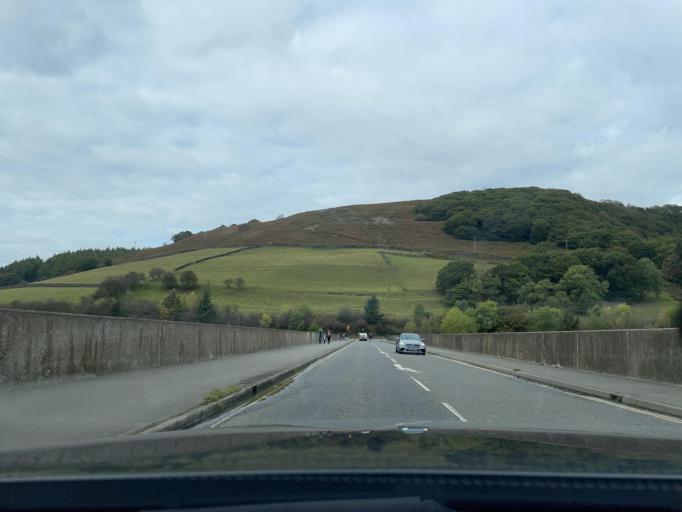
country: GB
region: England
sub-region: Derbyshire
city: Hope Valley
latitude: 53.3724
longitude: -1.6965
